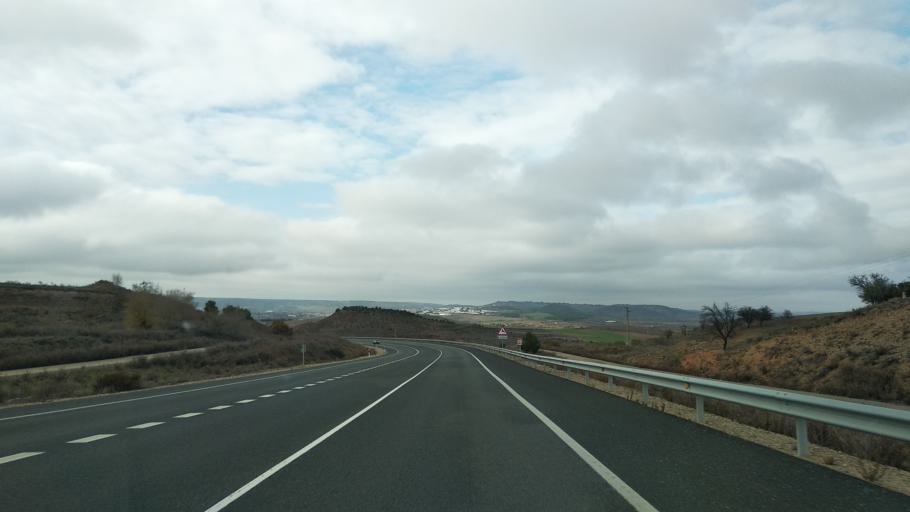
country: ES
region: La Rioja
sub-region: Provincia de La Rioja
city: Calahorra
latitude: 42.3211
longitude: -2.0149
